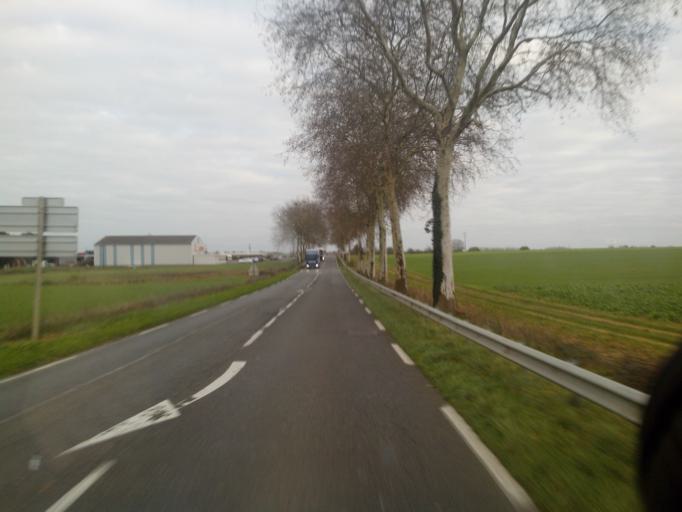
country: FR
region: Poitou-Charentes
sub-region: Departement de la Vienne
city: Ayron
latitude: 46.6598
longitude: 0.0542
